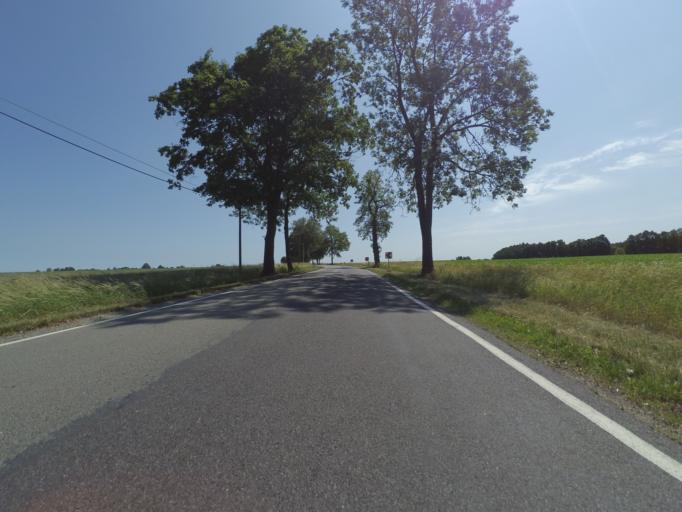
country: DE
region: Brandenburg
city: Gerdshagen
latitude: 53.3114
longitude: 12.2706
